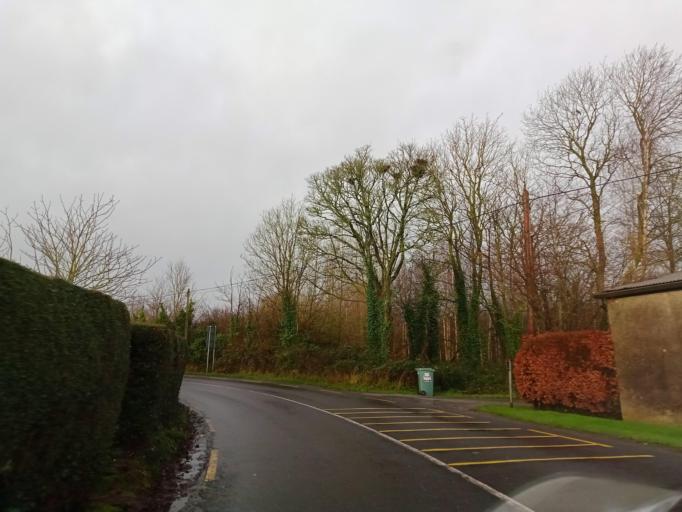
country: IE
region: Leinster
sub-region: Kilkenny
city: Callan
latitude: 52.5726
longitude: -7.4137
